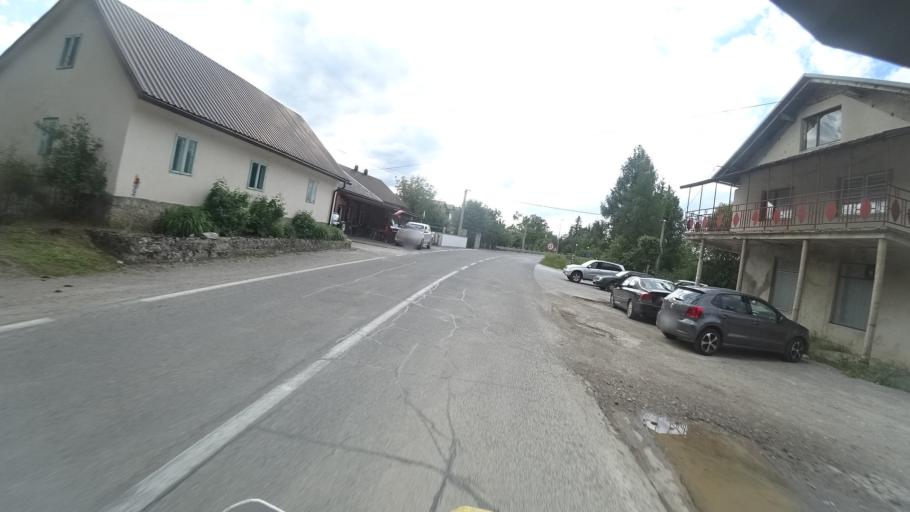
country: HR
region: Licko-Senjska
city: Gospic
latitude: 44.5137
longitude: 15.4243
